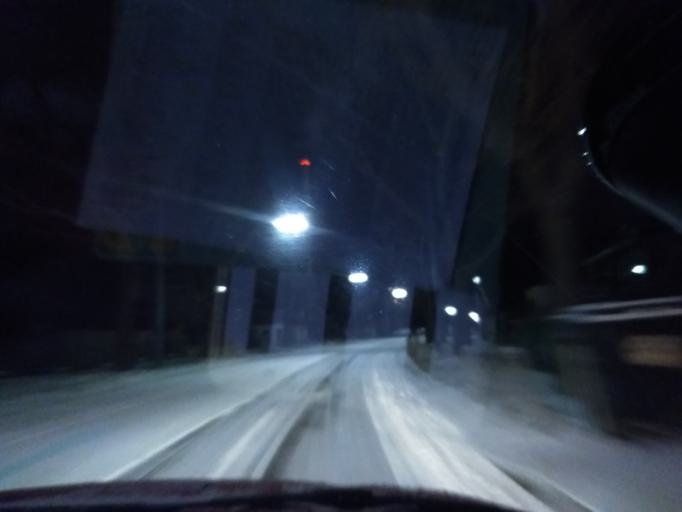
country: AT
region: Vienna
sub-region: Wien Stadt
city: Vienna
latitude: 48.2041
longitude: 16.2900
